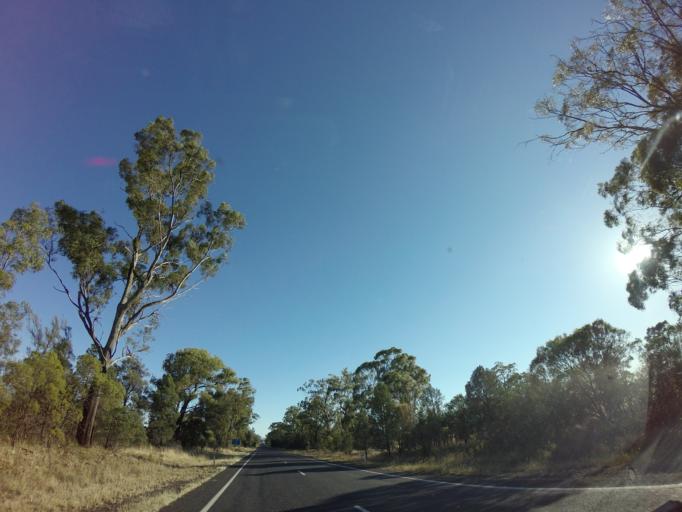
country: AU
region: New South Wales
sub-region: Gilgandra
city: Gilgandra
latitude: -31.5779
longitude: 148.7798
